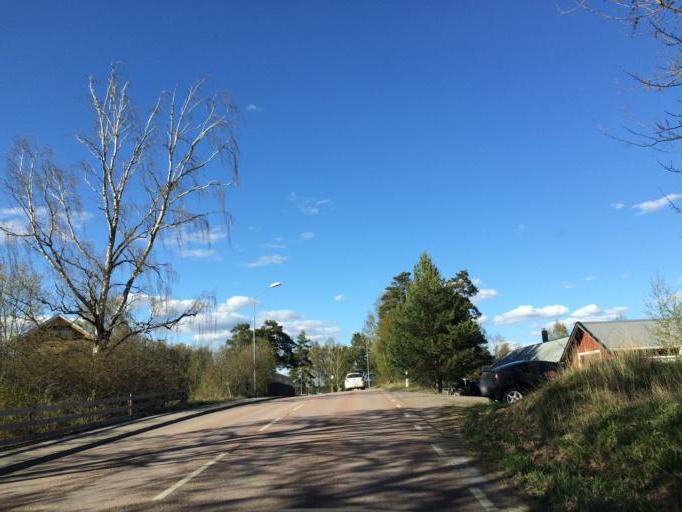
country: SE
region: Soedermanland
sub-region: Eskilstuna Kommun
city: Kvicksund
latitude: 59.4314
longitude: 16.3389
